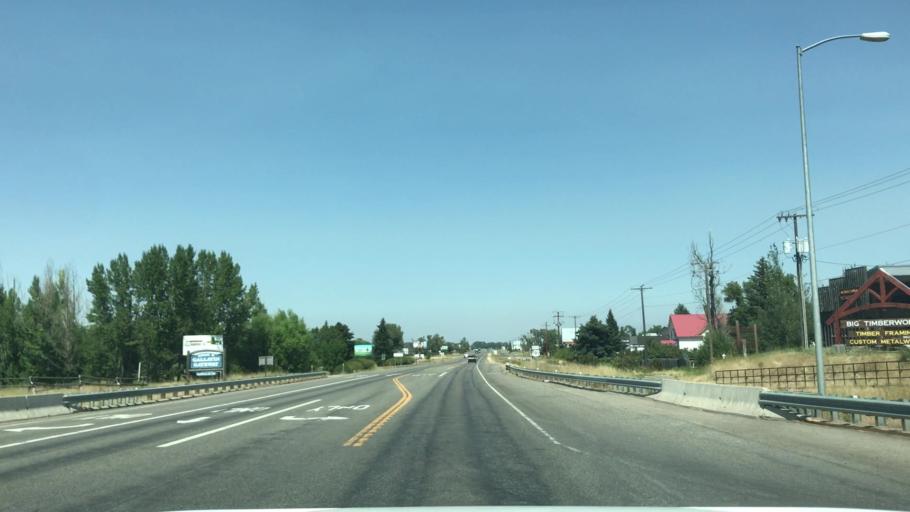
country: US
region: Montana
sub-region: Gallatin County
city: Four Corners
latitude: 45.5913
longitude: -111.1971
